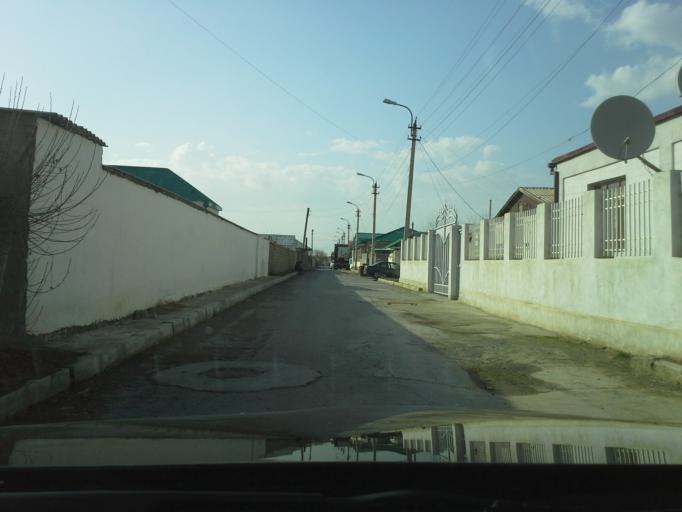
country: TM
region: Ahal
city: Abadan
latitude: 38.0177
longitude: 58.2361
